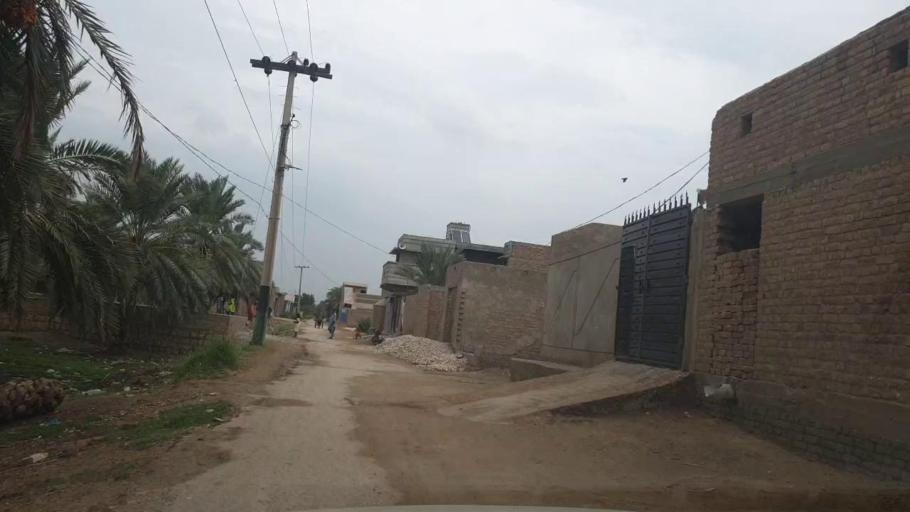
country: PK
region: Sindh
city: Khairpur
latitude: 27.5440
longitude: 68.7398
